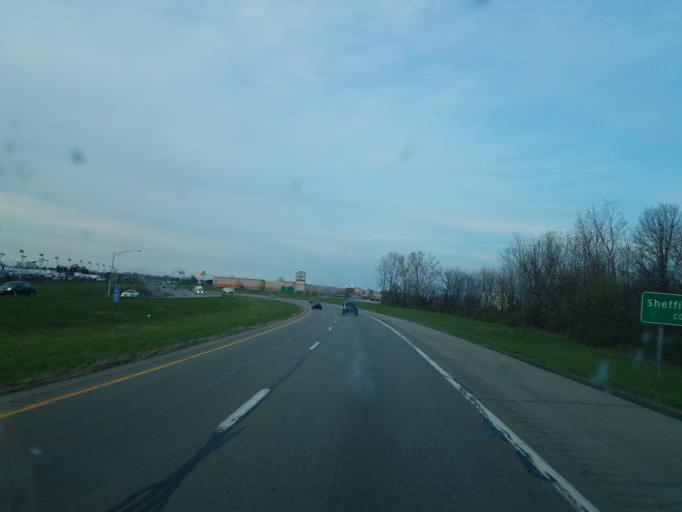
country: US
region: Ohio
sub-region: Lorain County
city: Sheffield
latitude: 41.4185
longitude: -82.0865
